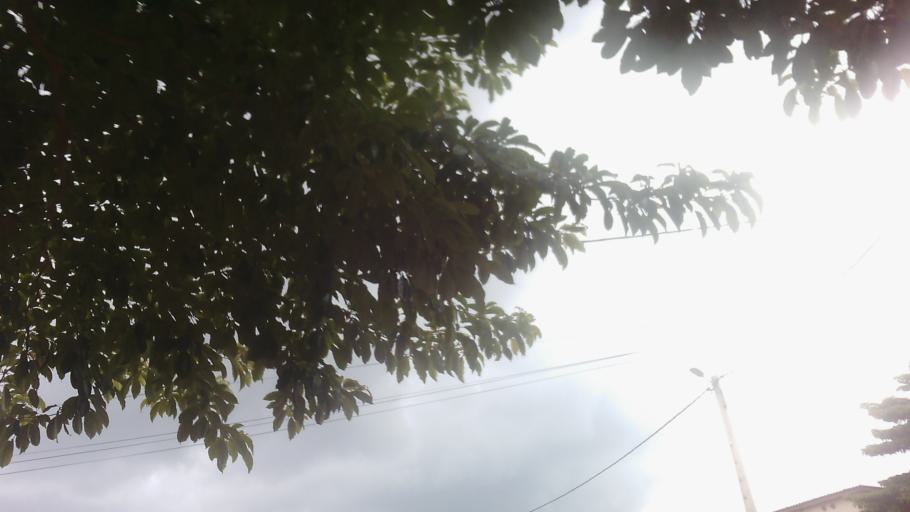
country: BJ
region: Atlantique
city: Abomey-Calavi
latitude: 6.4756
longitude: 2.3458
